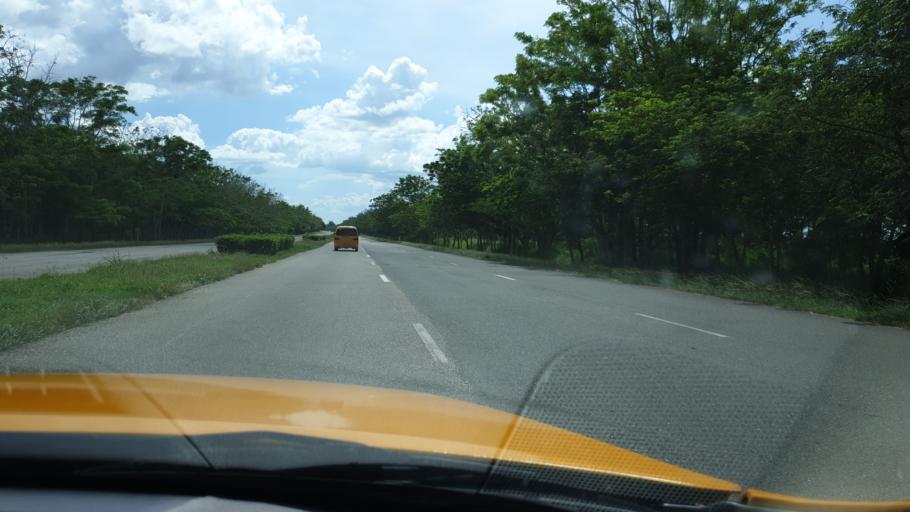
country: CU
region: Cienfuegos
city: Cruces
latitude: 22.4554
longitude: -80.3133
